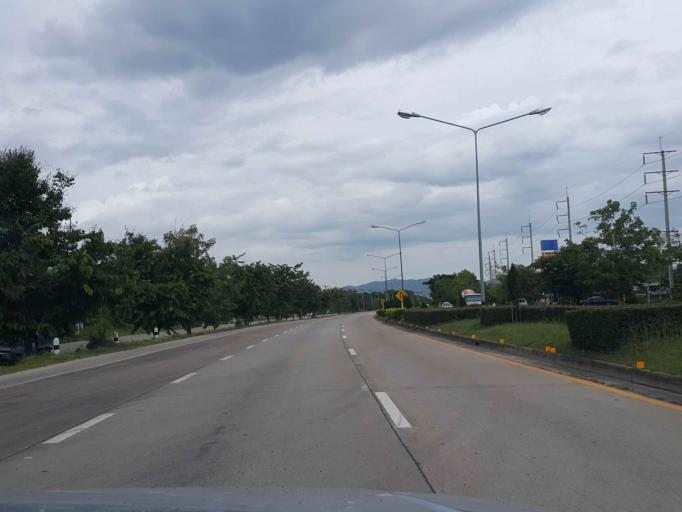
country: TH
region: Lampang
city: Lampang
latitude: 18.2883
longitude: 99.4431
